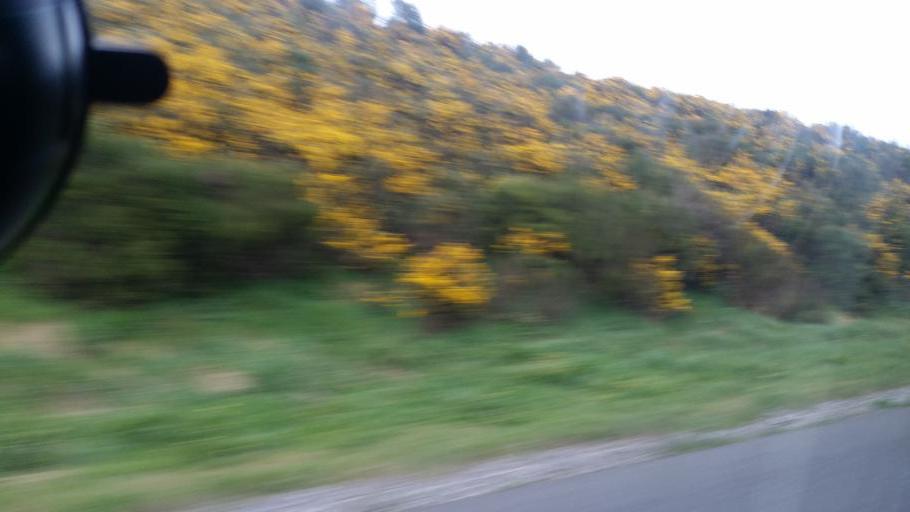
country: IE
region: Ulster
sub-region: An Cabhan
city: Belturbet
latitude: 54.0642
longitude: -7.3949
